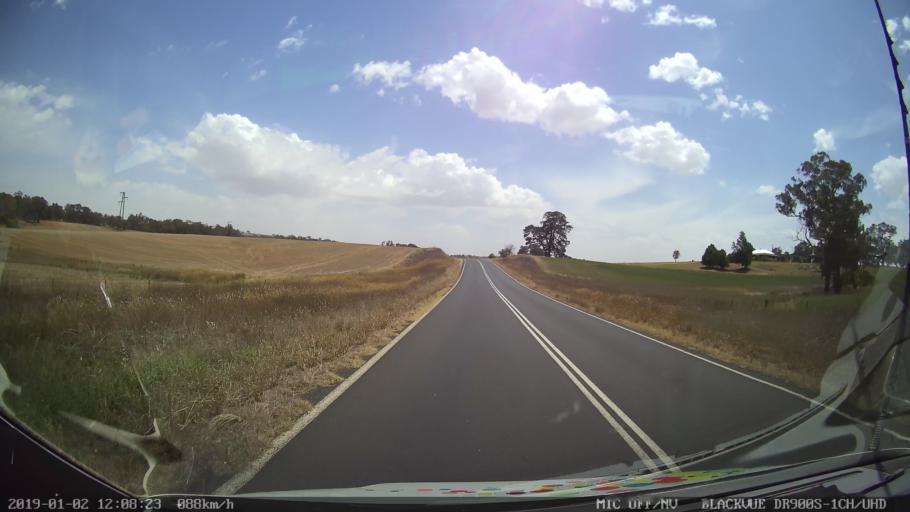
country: AU
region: New South Wales
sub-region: Young
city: Young
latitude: -34.4848
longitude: 148.2761
